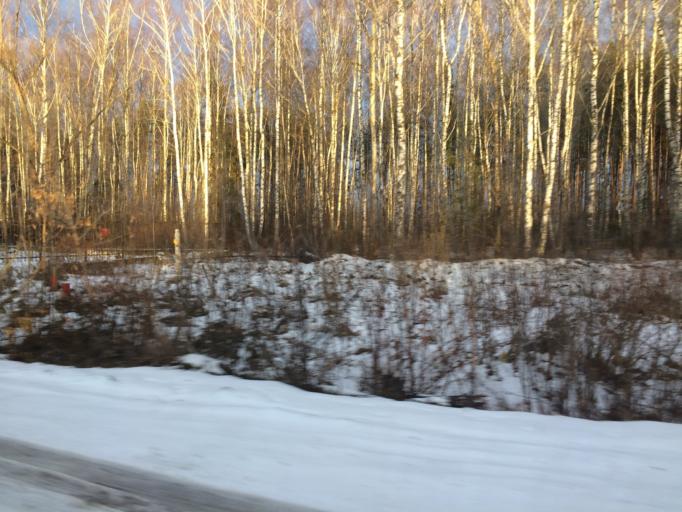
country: RU
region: Tula
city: Cherepet'
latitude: 54.1109
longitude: 36.3409
